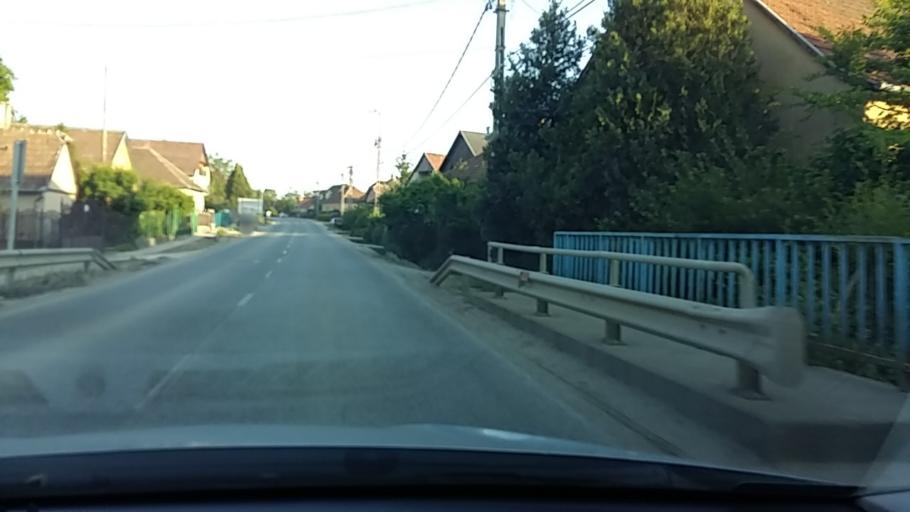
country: HU
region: Pest
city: Orbottyan
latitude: 47.6798
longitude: 19.2655
